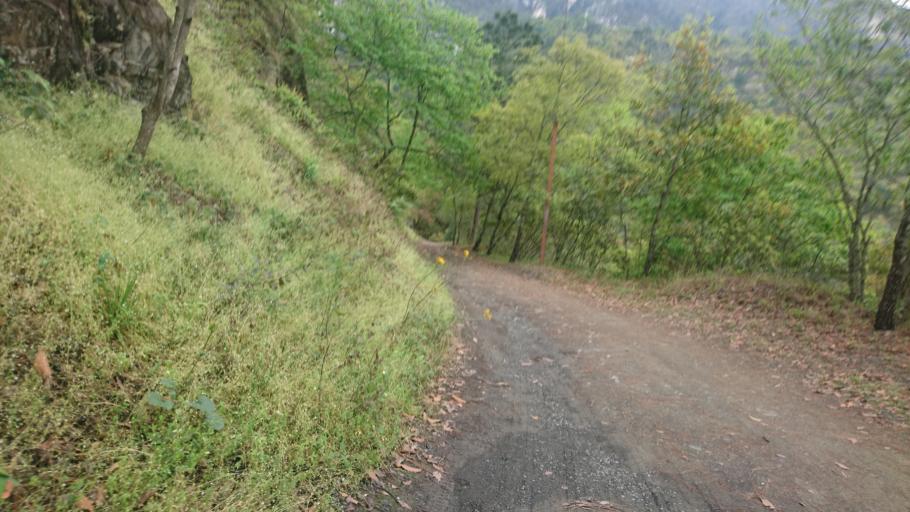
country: MX
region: Nuevo Leon
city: Garza Garcia
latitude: 25.6051
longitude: -100.3461
